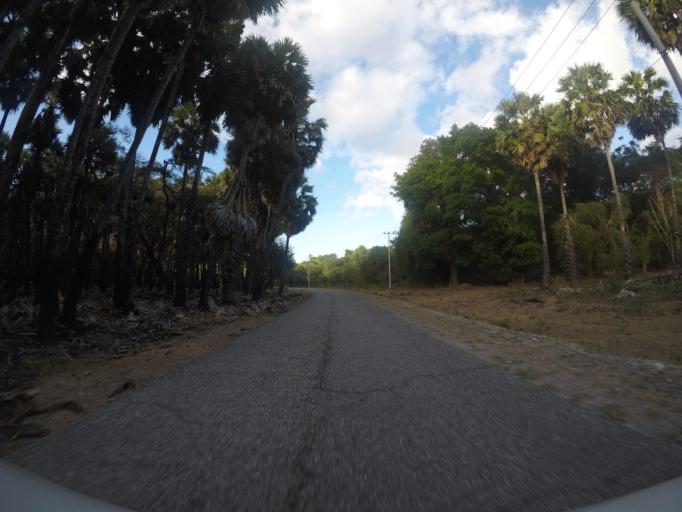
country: TL
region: Lautem
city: Lospalos
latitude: -8.3328
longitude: 126.9561
